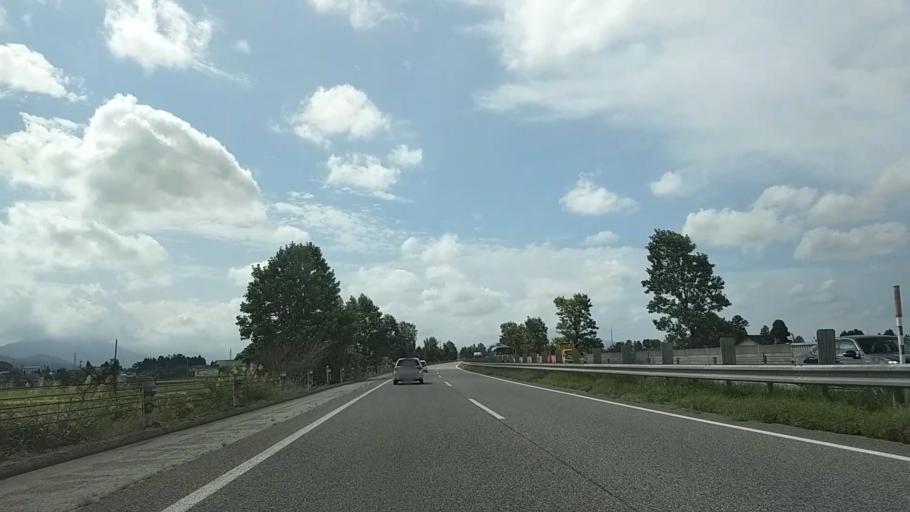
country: JP
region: Toyama
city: Takaoka
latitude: 36.6671
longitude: 137.0284
